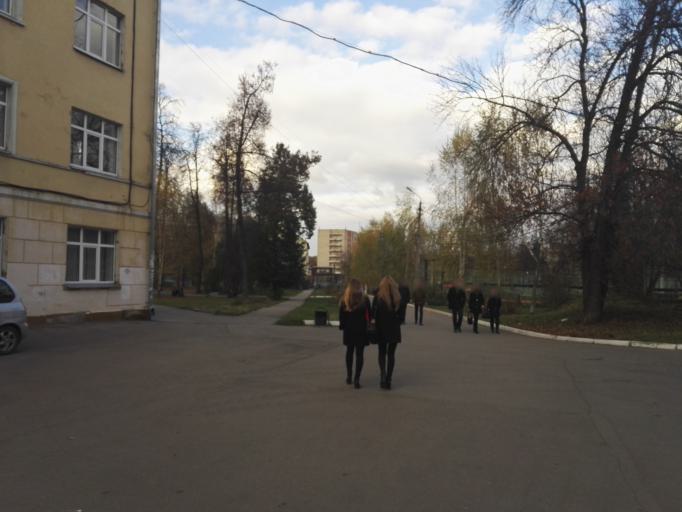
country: RU
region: Tula
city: Mendeleyevskiy
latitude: 54.1714
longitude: 37.5901
